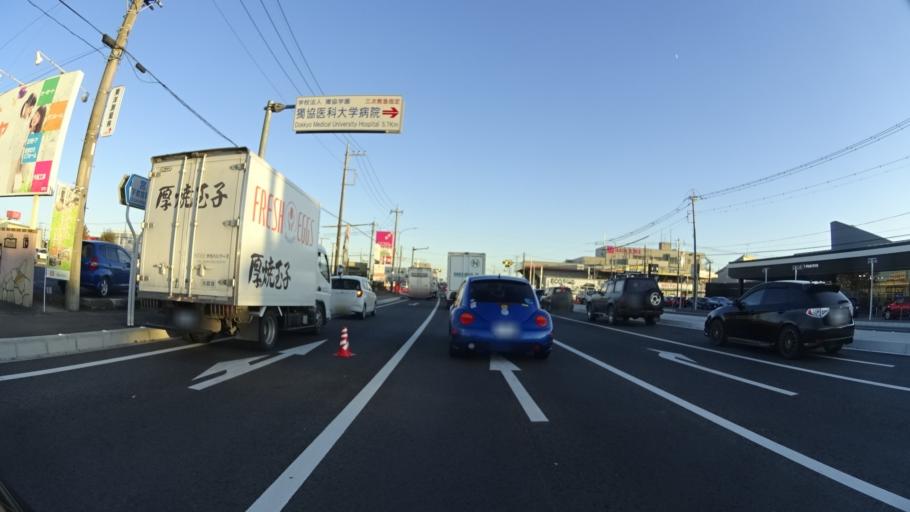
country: JP
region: Tochigi
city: Utsunomiya-shi
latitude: 36.5167
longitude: 139.8431
